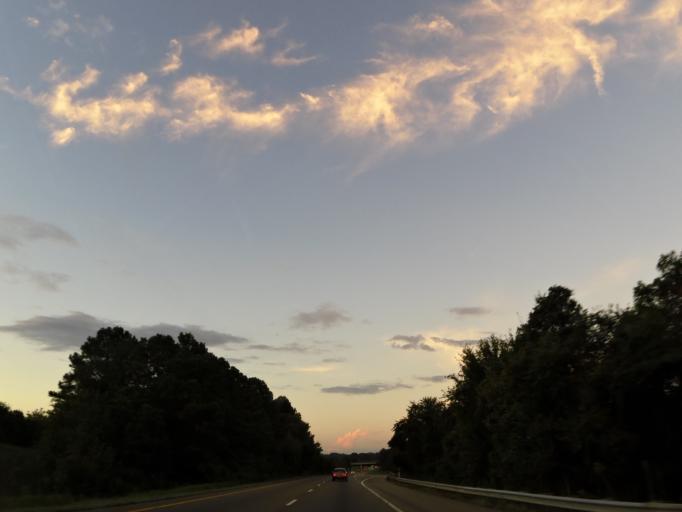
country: US
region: Tennessee
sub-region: Loudon County
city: Loudon
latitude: 35.7789
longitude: -84.3489
